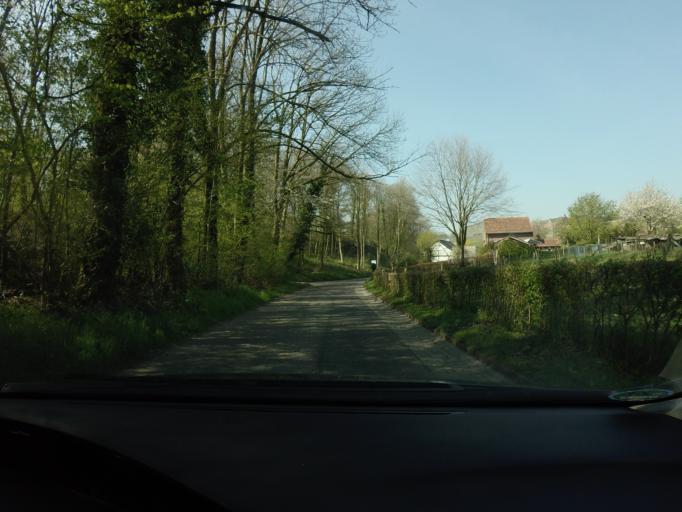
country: NL
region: Limburg
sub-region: Valkenburg aan de Geul
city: Houthem
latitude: 50.8955
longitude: 5.7807
